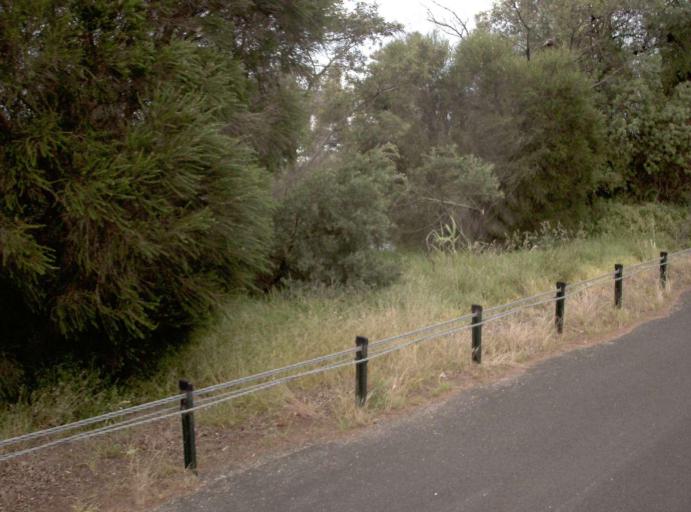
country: AU
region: Victoria
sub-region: East Gippsland
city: Bairnsdale
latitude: -37.8688
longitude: 147.6492
